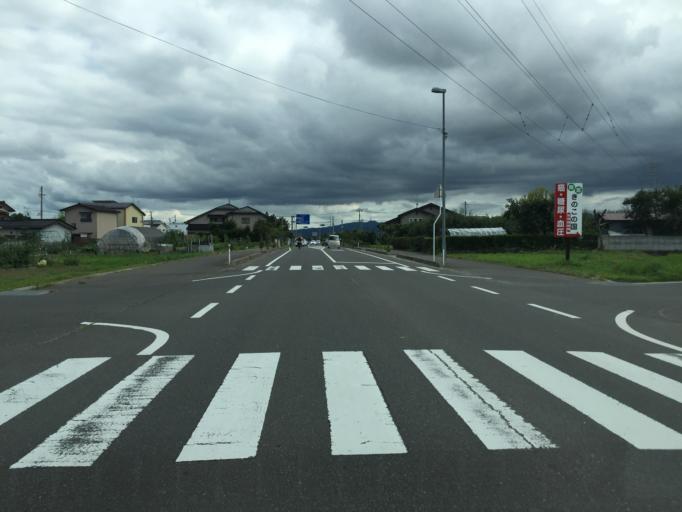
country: JP
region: Fukushima
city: Fukushima-shi
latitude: 37.7919
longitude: 140.4281
